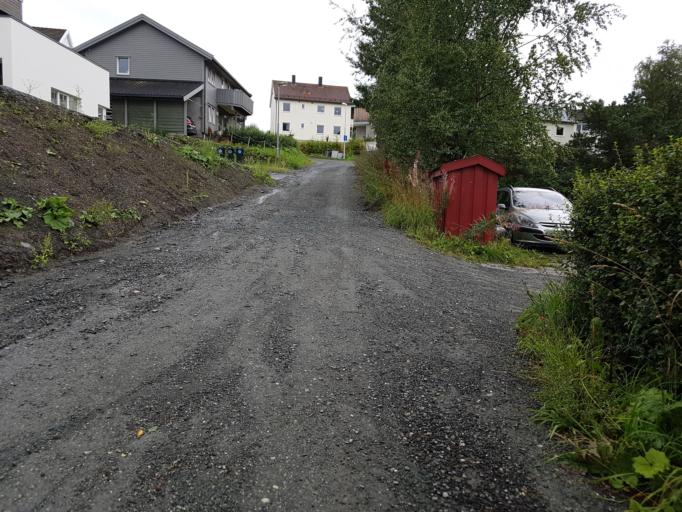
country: NO
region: Sor-Trondelag
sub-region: Trondheim
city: Trondheim
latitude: 63.3943
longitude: 10.4071
